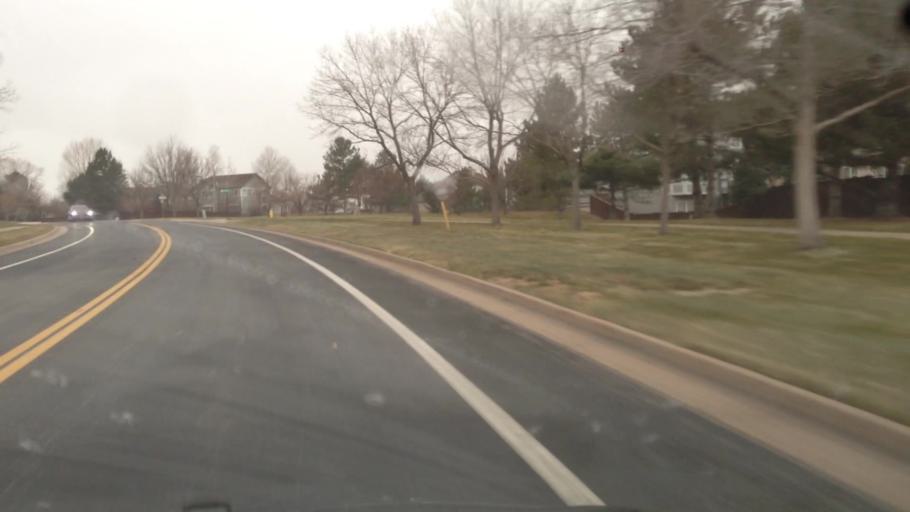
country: US
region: Colorado
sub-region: Douglas County
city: Stonegate
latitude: 39.5243
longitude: -104.7963
